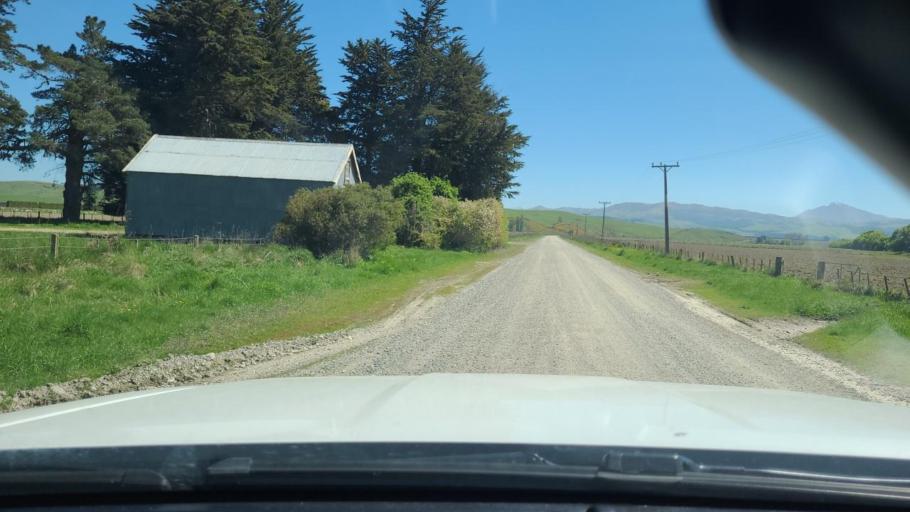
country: NZ
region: Southland
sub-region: Gore District
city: Gore
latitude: -45.7432
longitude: 168.8217
